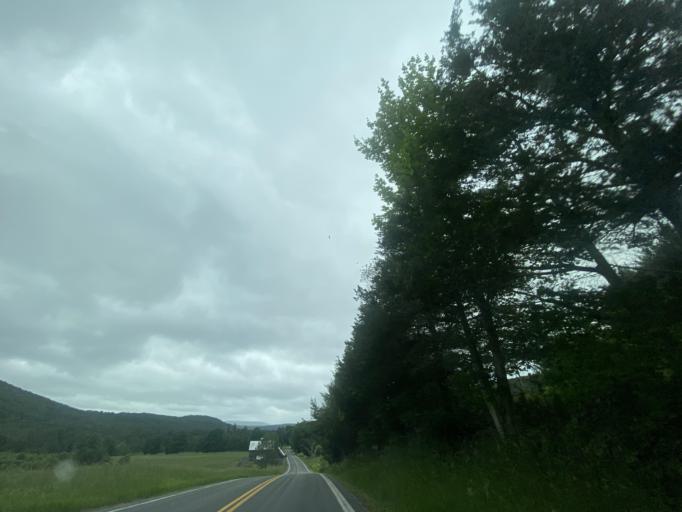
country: US
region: New York
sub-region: Delaware County
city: Stamford
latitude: 42.3806
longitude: -74.3961
